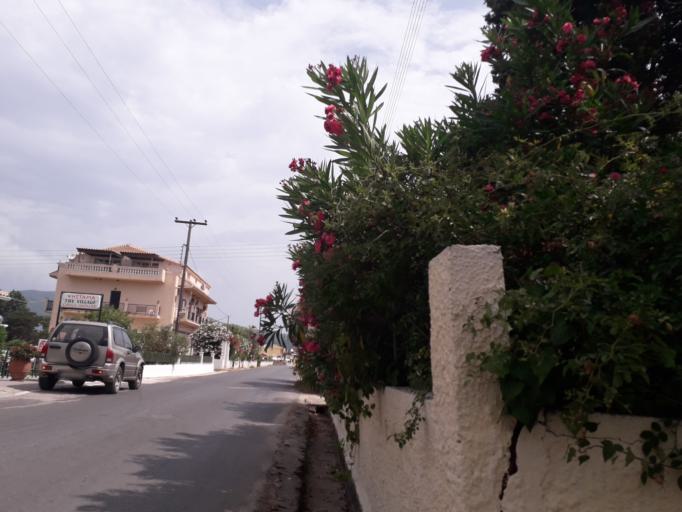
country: GR
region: Ionian Islands
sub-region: Nomos Kerkyras
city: Perivoli
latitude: 39.4263
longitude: 19.9476
